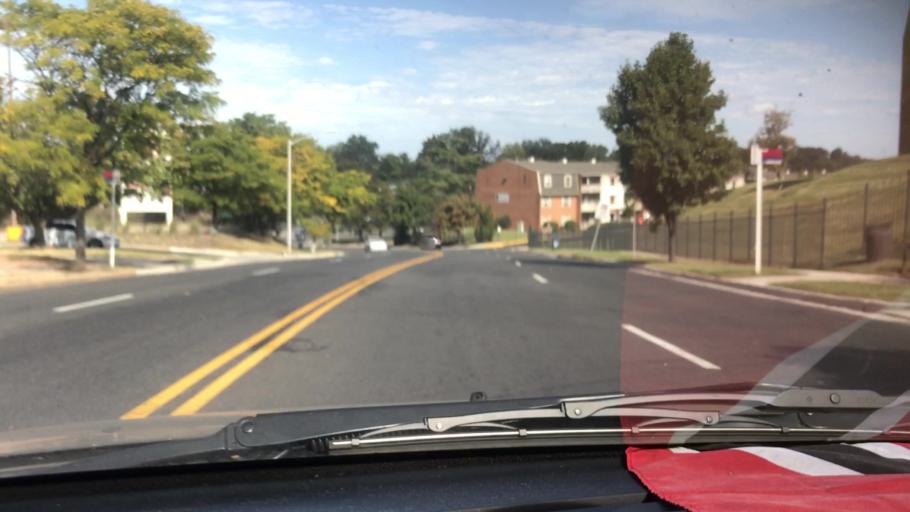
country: US
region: Maryland
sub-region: Prince George's County
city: Peppermill Village
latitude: 38.9149
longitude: -76.8822
